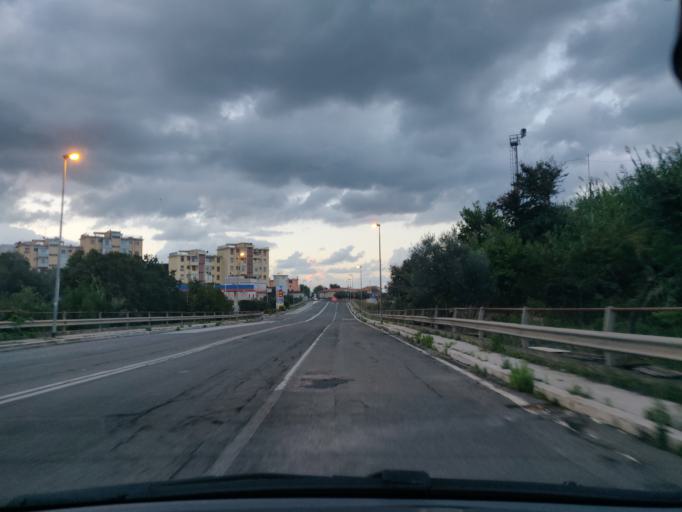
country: IT
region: Latium
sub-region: Citta metropolitana di Roma Capitale
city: Civitavecchia
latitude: 42.0832
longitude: 11.8085
